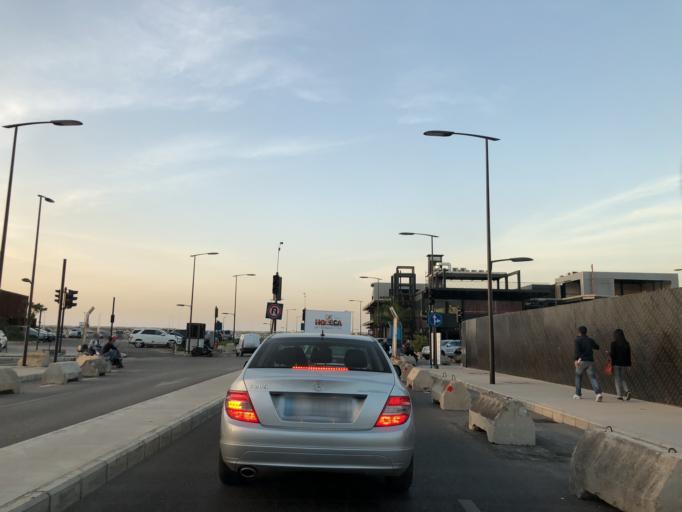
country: LB
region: Beyrouth
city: Beirut
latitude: 33.9052
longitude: 35.5060
